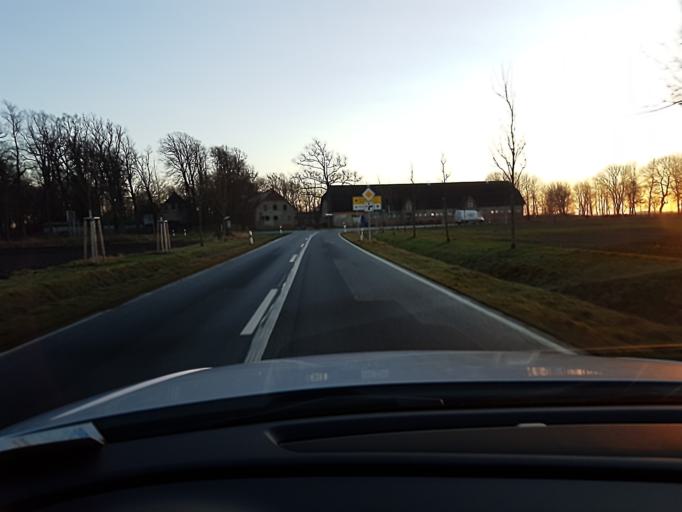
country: DE
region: Mecklenburg-Vorpommern
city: Wiek
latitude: 54.5878
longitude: 13.2882
